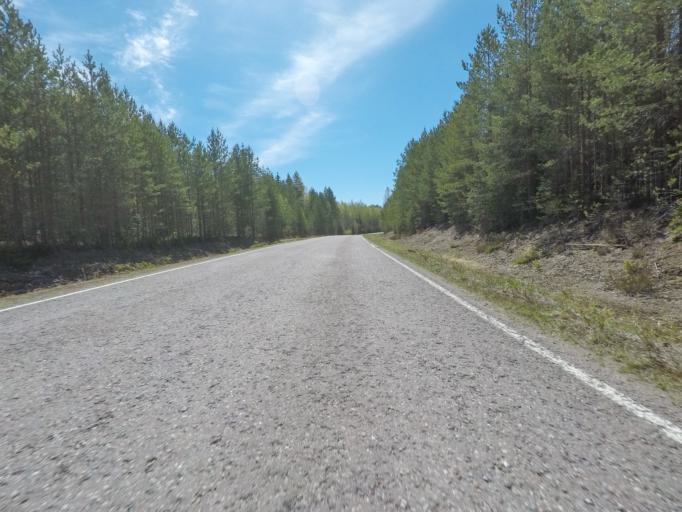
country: FI
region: Uusimaa
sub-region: Helsinki
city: Kaerkoelae
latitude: 60.5927
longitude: 23.7999
